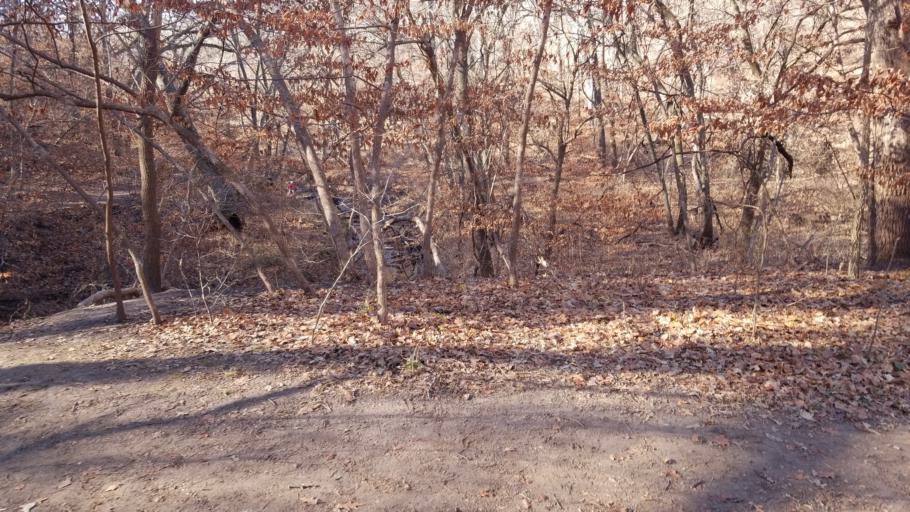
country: US
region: Nebraska
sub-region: Cass County
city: Louisville
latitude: 40.9914
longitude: -96.2162
